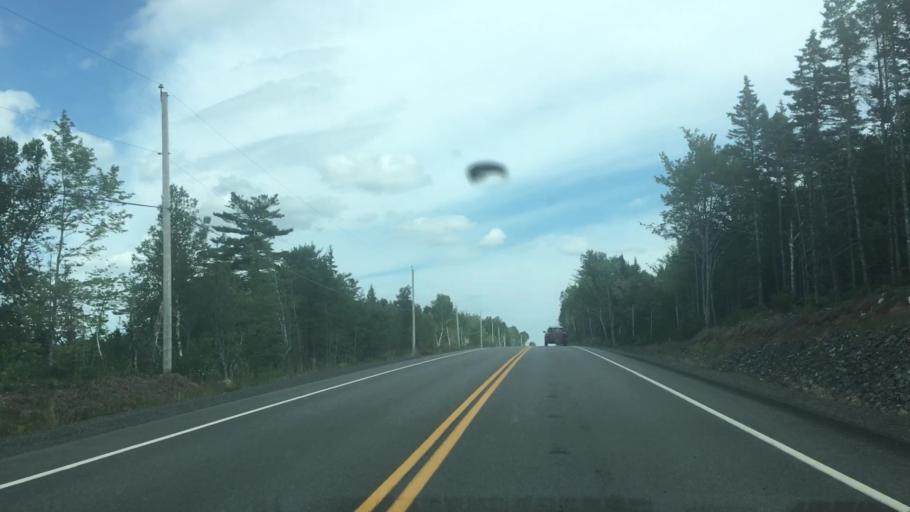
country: CA
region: Nova Scotia
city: Sydney Mines
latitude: 46.3119
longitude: -60.6147
